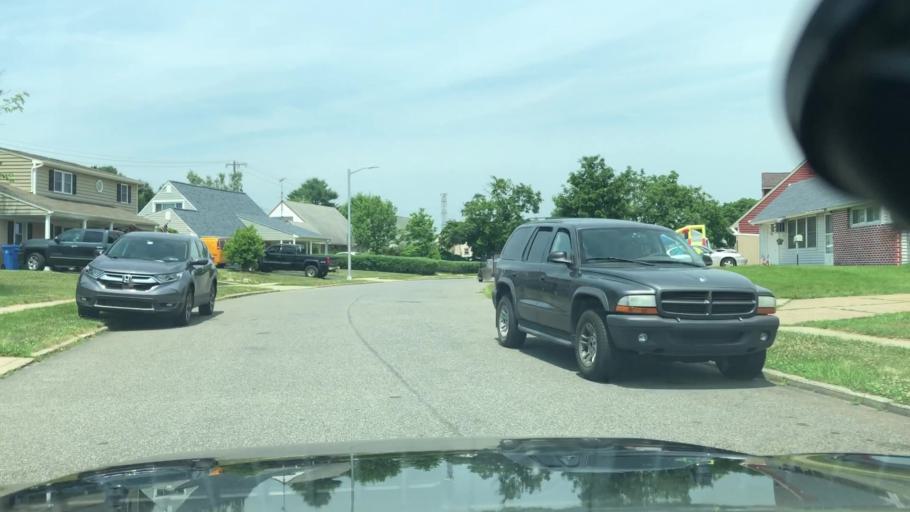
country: US
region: Pennsylvania
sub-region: Bucks County
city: Tullytown
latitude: 40.1360
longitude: -74.8308
